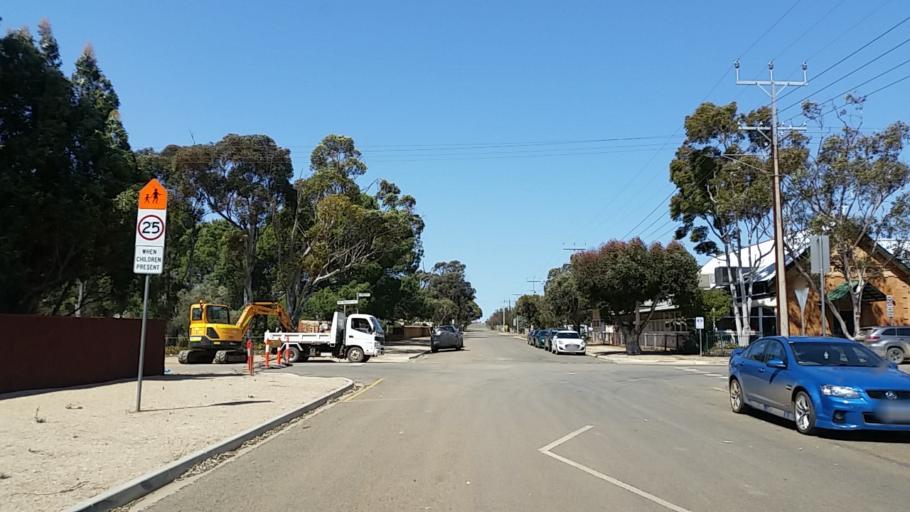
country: AU
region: South Australia
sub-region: Peterborough
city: Peterborough
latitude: -32.9750
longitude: 138.8423
